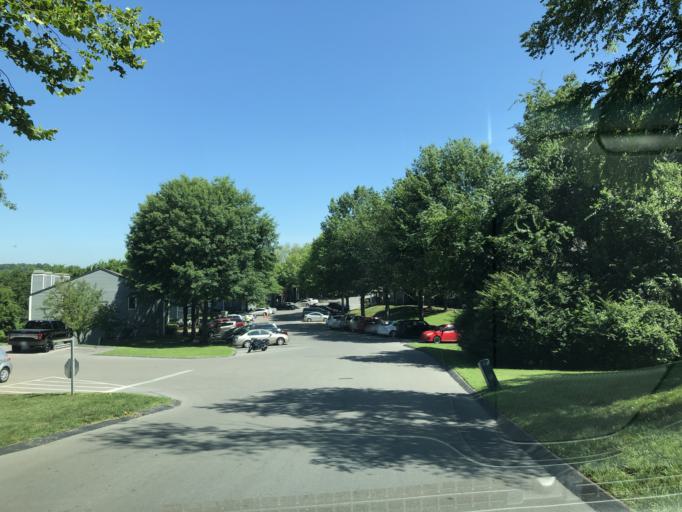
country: US
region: Tennessee
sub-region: Williamson County
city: Nolensville
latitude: 36.0390
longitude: -86.6691
